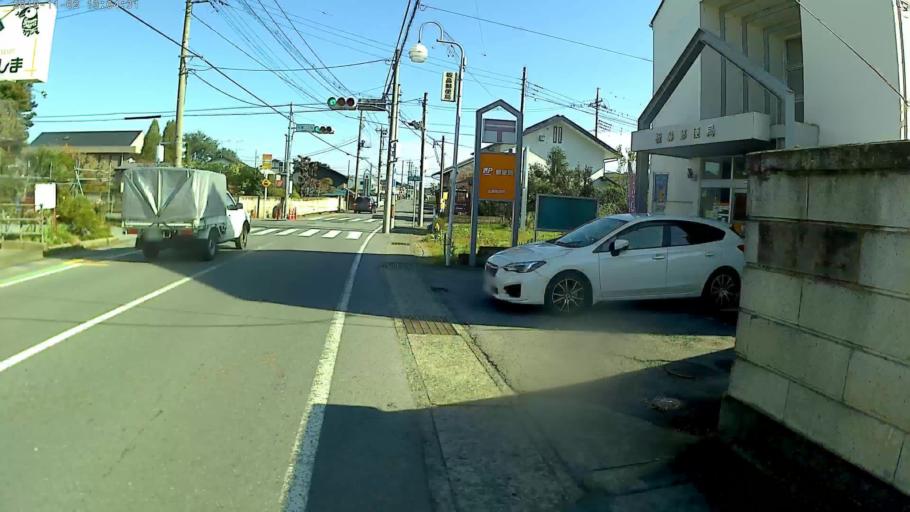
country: JP
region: Gunma
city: Annaka
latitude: 36.3371
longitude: 138.9339
